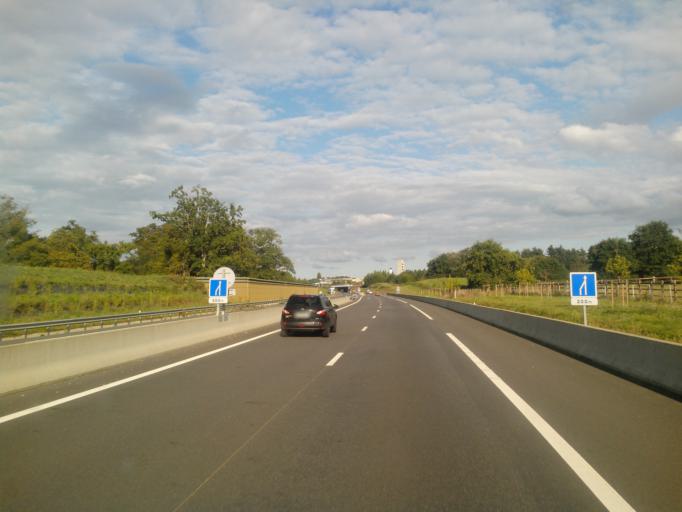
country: FR
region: Brittany
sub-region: Departement d'Ille-et-Vilaine
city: Montgermont
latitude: 48.1257
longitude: -1.7237
